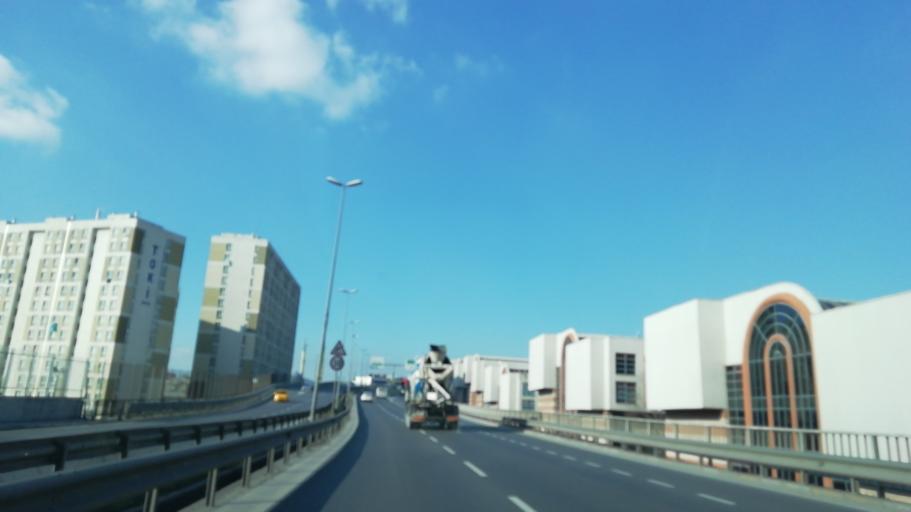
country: TR
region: Istanbul
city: Esenler
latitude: 41.0656
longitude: 28.8633
